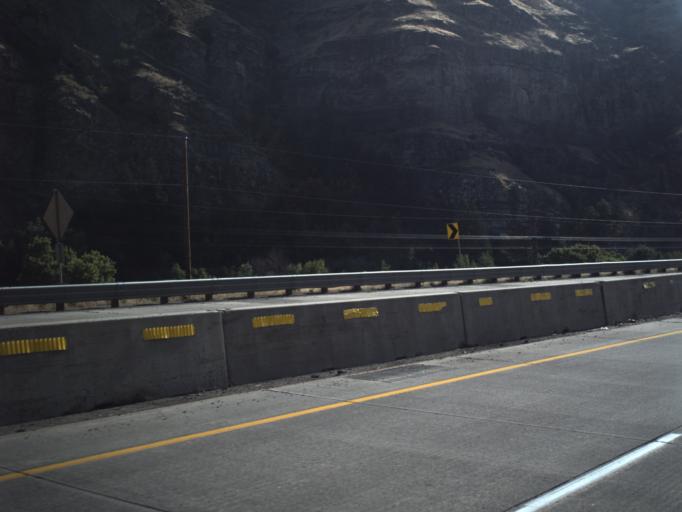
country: US
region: Utah
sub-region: Morgan County
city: Morgan
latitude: 41.0533
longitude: -111.5949
